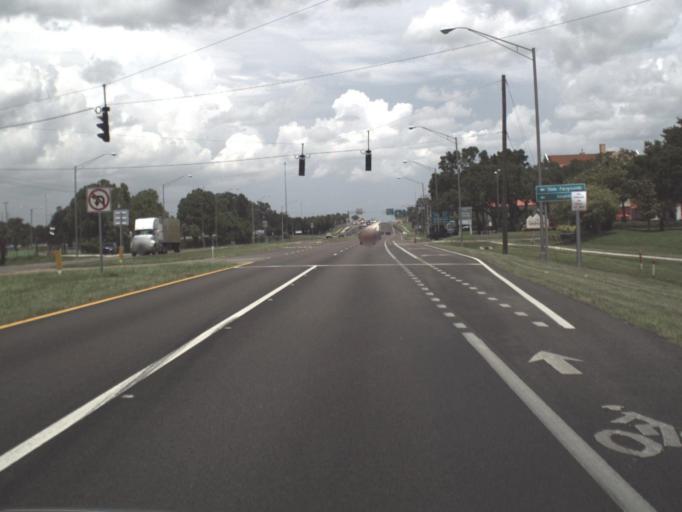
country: US
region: Florida
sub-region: Hillsborough County
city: East Lake-Orient Park
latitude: 27.9891
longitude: -82.3587
